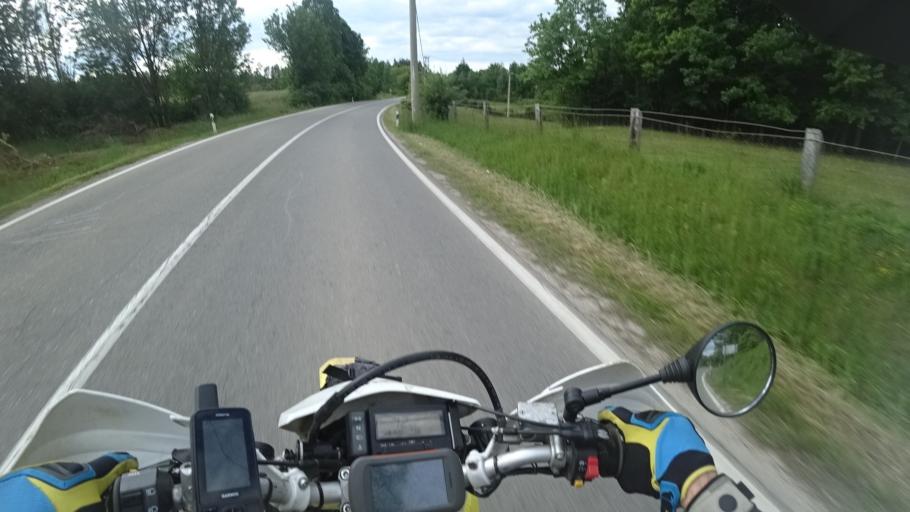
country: HR
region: Licko-Senjska
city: Gospic
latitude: 44.5177
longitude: 15.4167
